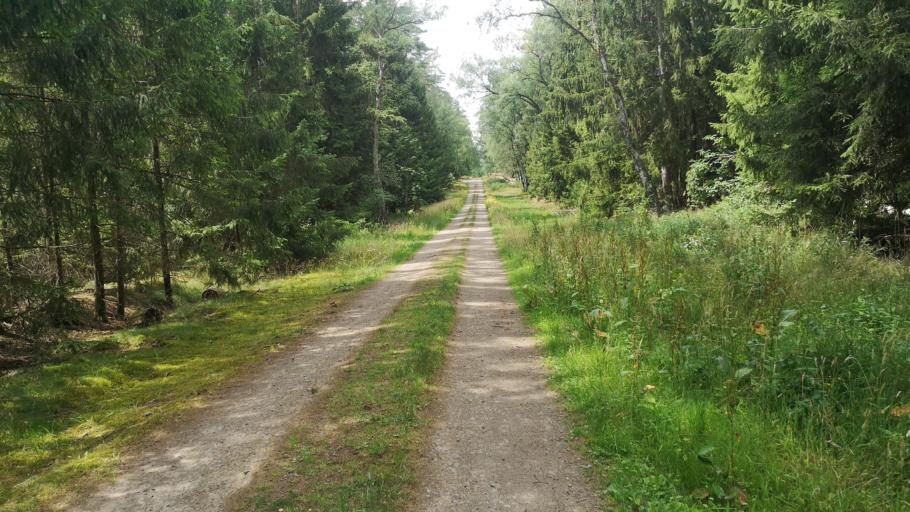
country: DE
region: Lower Saxony
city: Thomasburg
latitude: 53.2367
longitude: 10.7151
